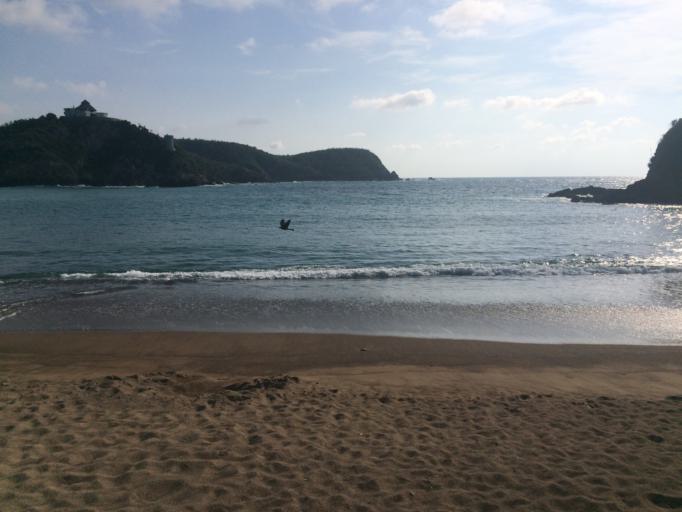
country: MX
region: Jalisco
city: Las Juntas
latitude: 19.4377
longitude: -105.0264
